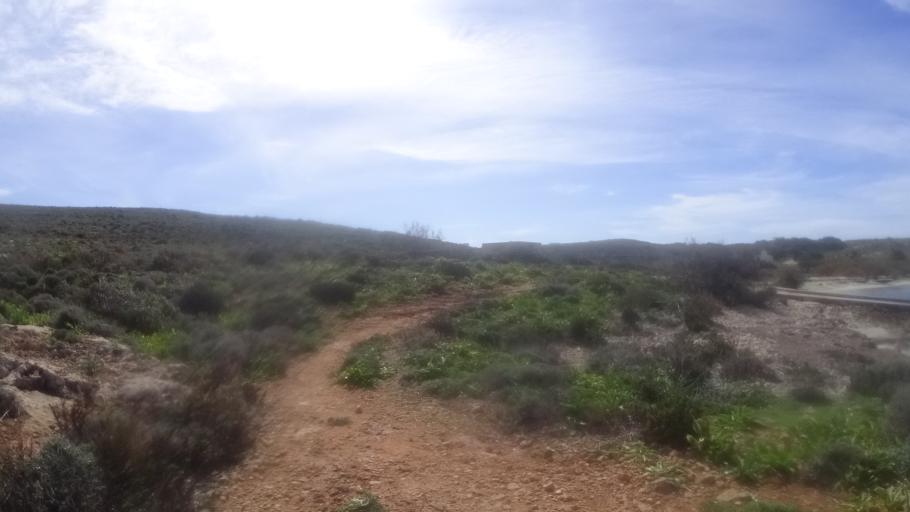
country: MT
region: Il-Qala
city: Qala
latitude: 36.0167
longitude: 14.3381
